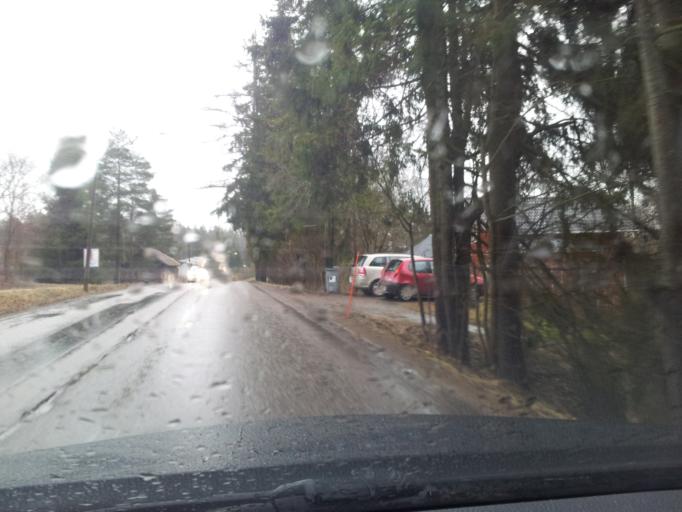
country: FI
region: Uusimaa
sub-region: Helsinki
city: Kirkkonummi
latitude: 60.1381
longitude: 24.5102
